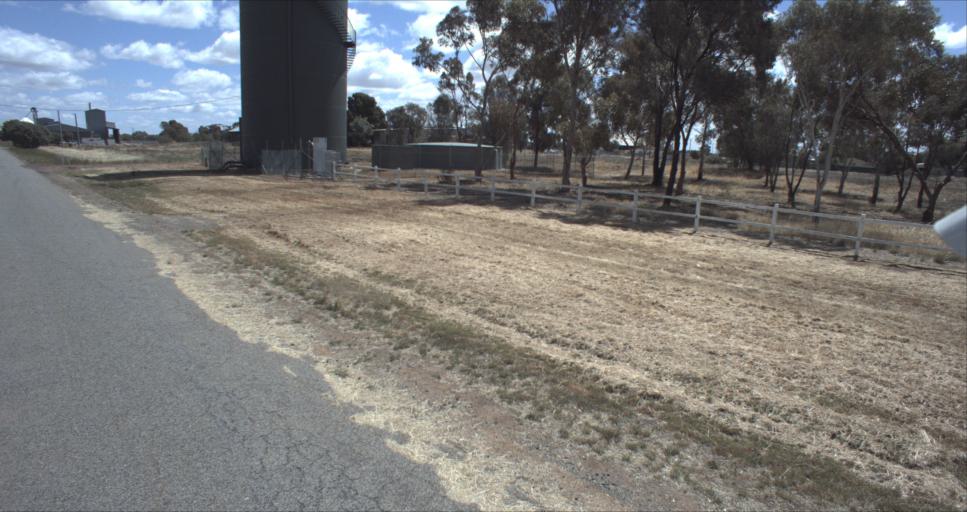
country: AU
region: New South Wales
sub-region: Murrumbidgee Shire
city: Darlington Point
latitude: -34.5170
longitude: 146.1825
